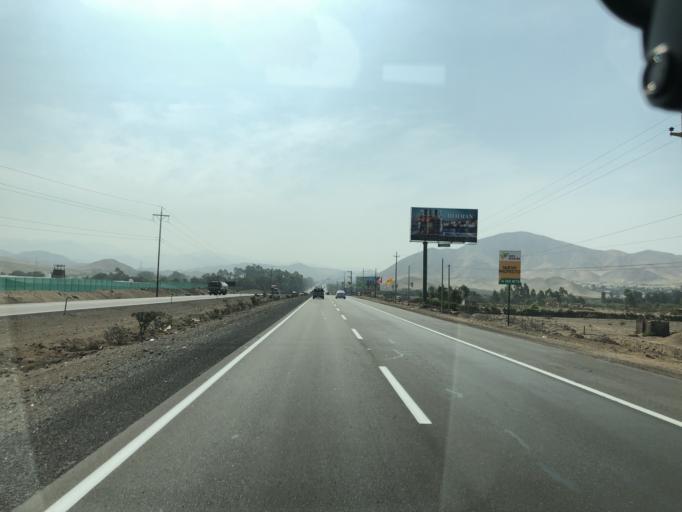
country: PE
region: Lima
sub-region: Provincia de Canete
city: Chilca
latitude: -12.5759
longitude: -76.6874
